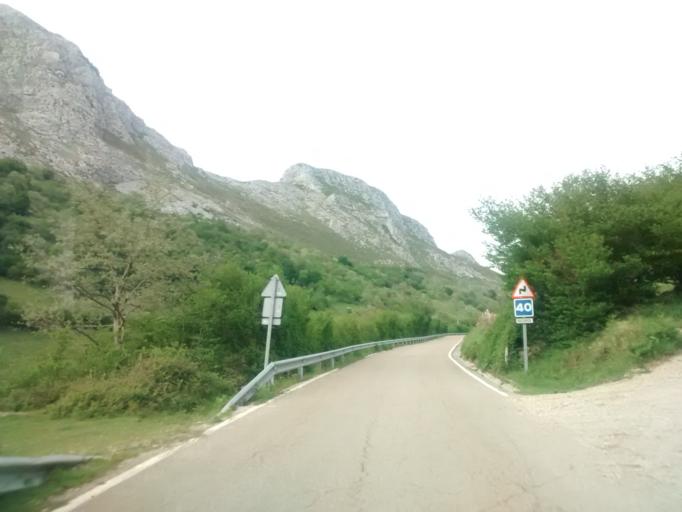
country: ES
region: Cantabria
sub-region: Provincia de Cantabria
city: San Vicente de la Barquera
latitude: 43.2543
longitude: -4.4548
